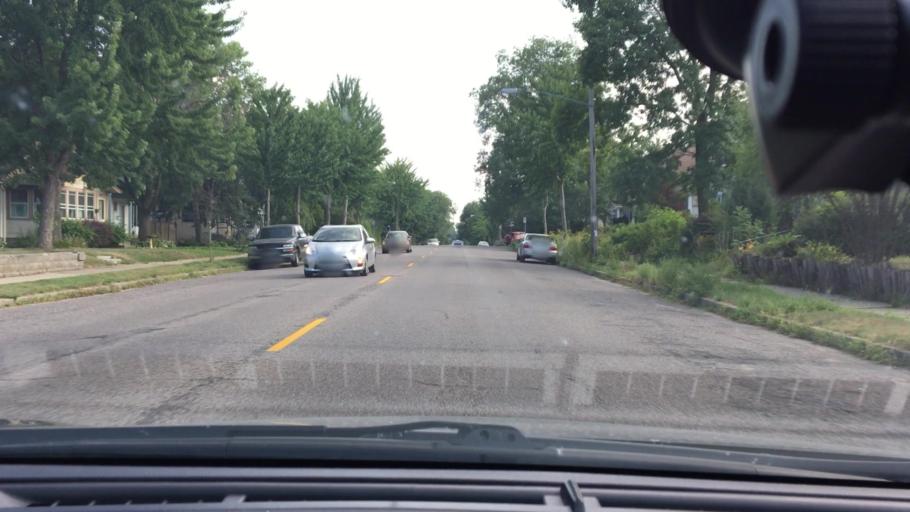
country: US
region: Minnesota
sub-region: Hennepin County
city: Minneapolis
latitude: 44.9333
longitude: -93.2525
